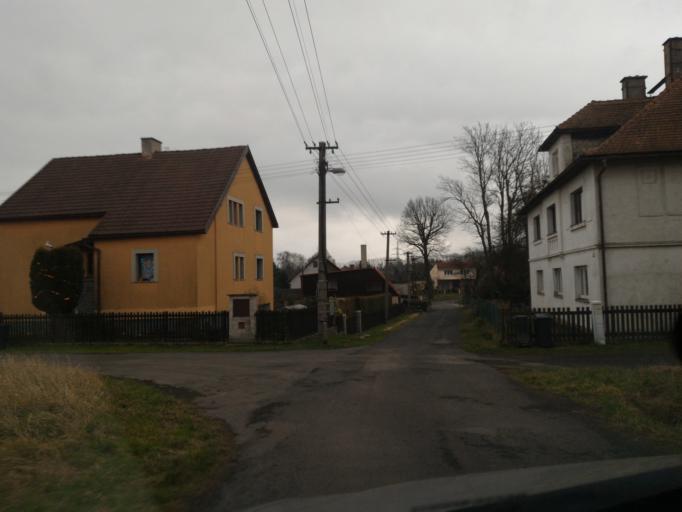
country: CZ
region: Ustecky
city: Varnsdorf
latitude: 50.9065
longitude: 14.6079
